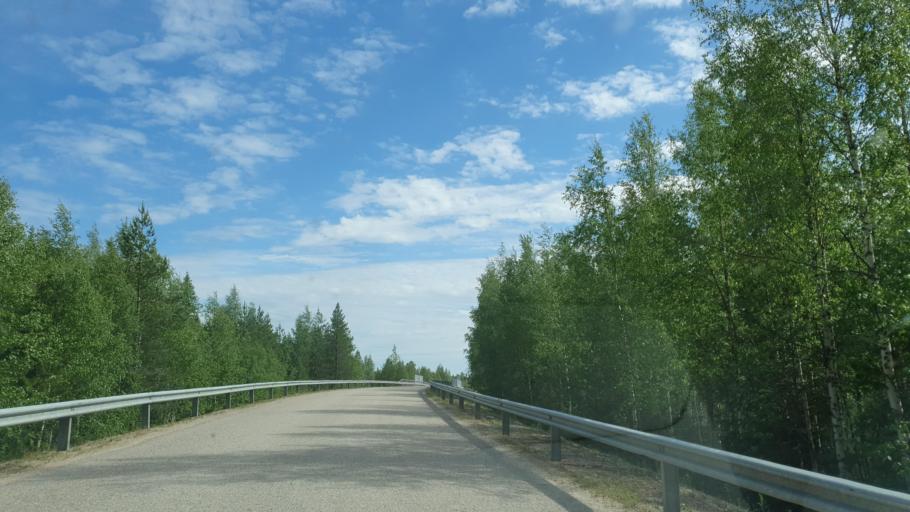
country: FI
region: Kainuu
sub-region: Kehys-Kainuu
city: Kuhmo
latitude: 64.4856
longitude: 29.5230
